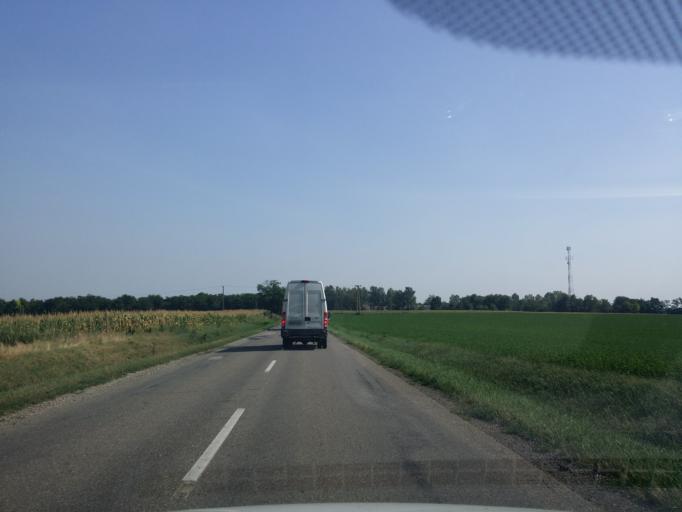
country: HU
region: Fejer
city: Mezofalva
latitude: 46.9389
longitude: 18.7493
